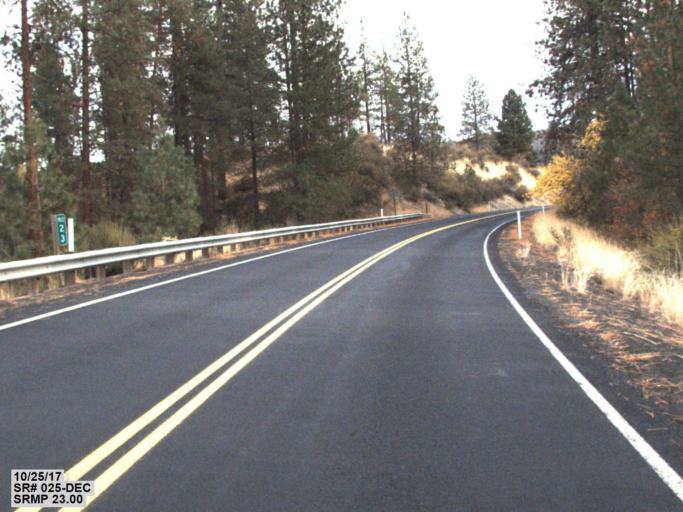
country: US
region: Washington
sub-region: Lincoln County
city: Davenport
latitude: 47.9079
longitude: -118.3082
